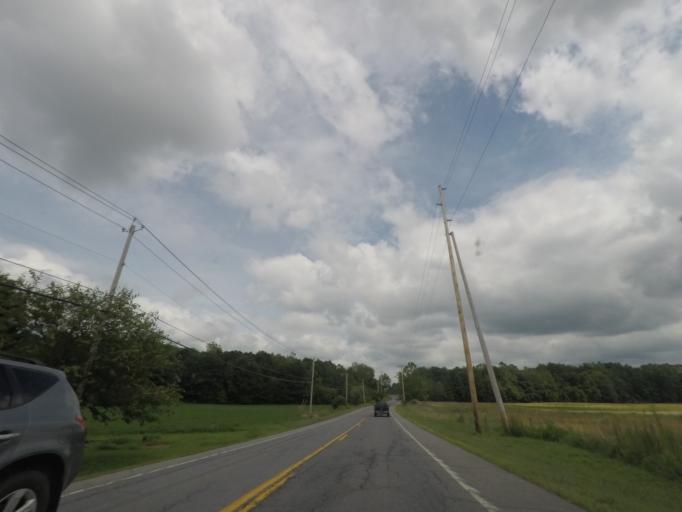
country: US
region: New York
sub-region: Saratoga County
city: Stillwater
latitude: 42.9099
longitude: -73.6210
